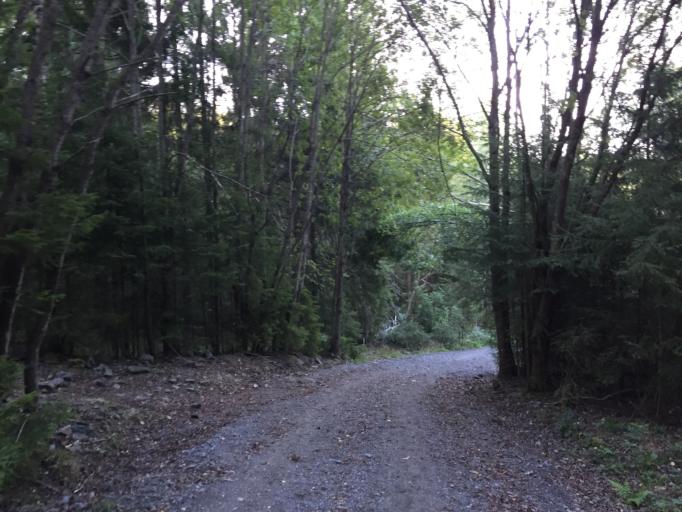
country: NO
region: Akershus
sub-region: Raelingen
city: Fjerdingby
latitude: 59.9294
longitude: 11.0475
